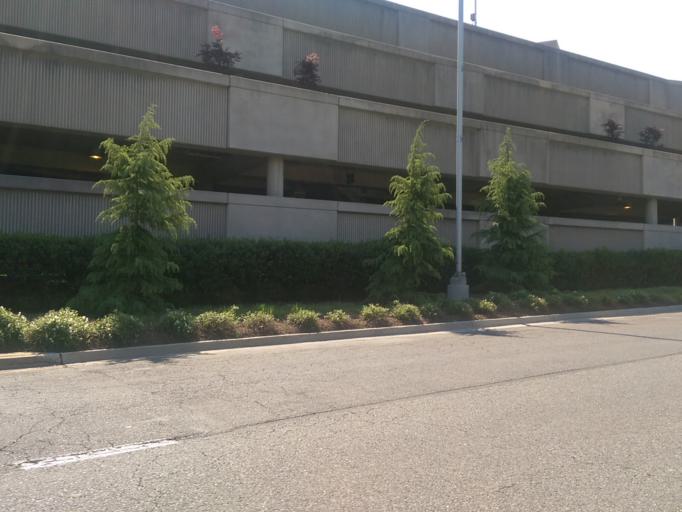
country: US
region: Washington, D.C.
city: Washington, D.C.
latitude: 38.8542
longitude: -77.0459
